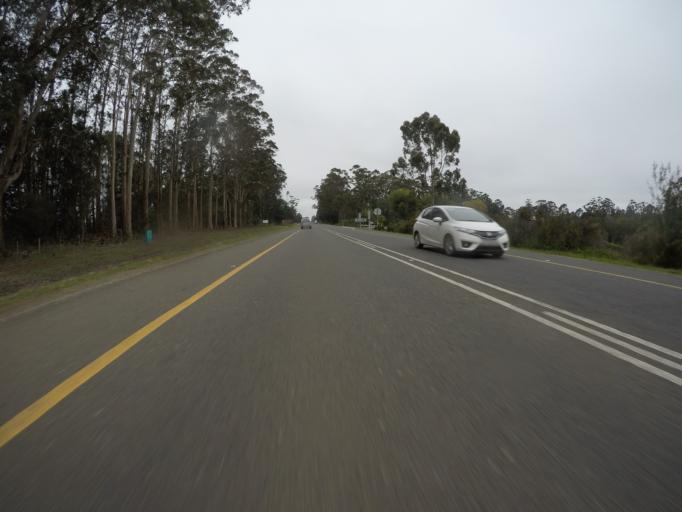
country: ZA
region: Western Cape
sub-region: Eden District Municipality
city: Plettenberg Bay
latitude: -34.0443
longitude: 23.2690
